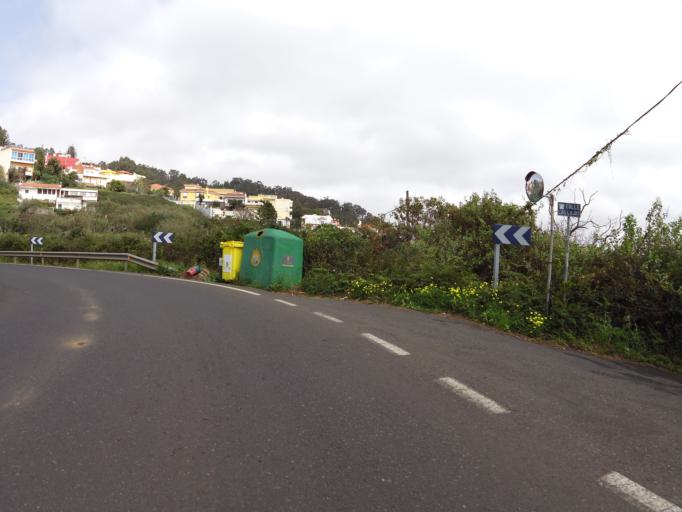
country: ES
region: Canary Islands
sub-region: Provincia de Las Palmas
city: Teror
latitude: 28.0838
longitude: -15.5409
